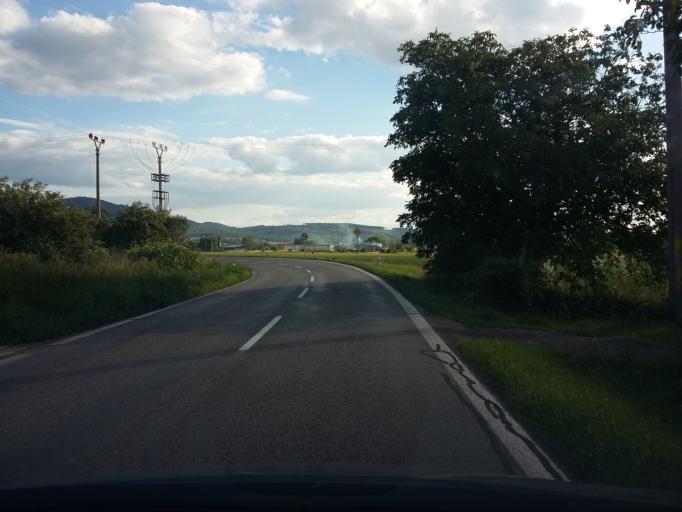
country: SK
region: Bratislavsky
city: Modra
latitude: 48.4864
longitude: 17.2549
